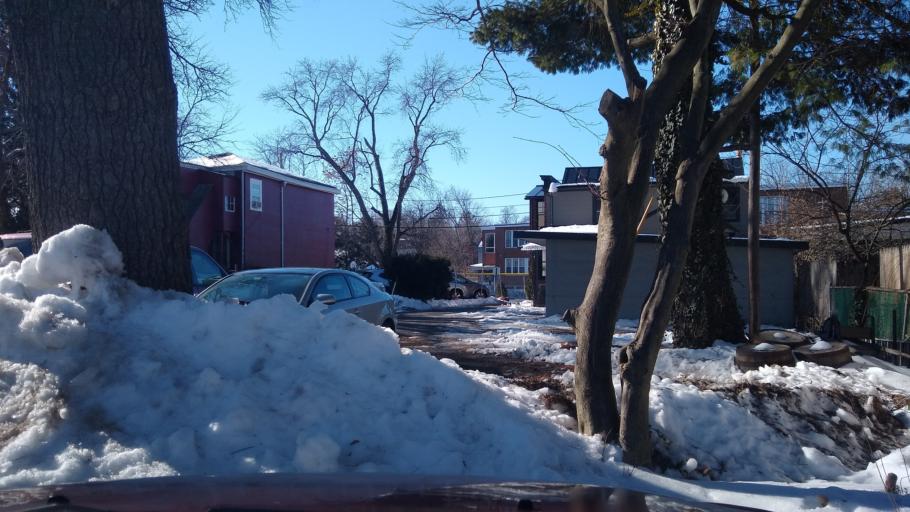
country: US
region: New York
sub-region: Ulster County
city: Kingston
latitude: 41.9314
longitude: -74.0181
